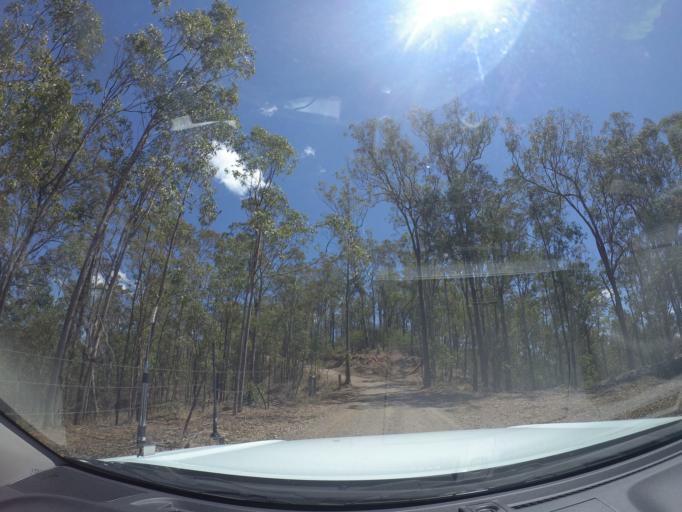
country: AU
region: Queensland
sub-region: Ipswich
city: Deebing Heights
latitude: -27.8325
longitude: 152.8260
